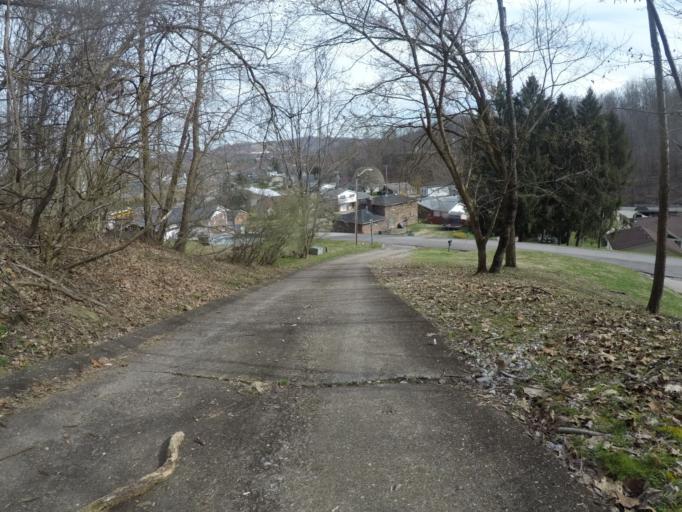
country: US
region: West Virginia
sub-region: Cabell County
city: Barboursville
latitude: 38.3993
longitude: -82.2945
